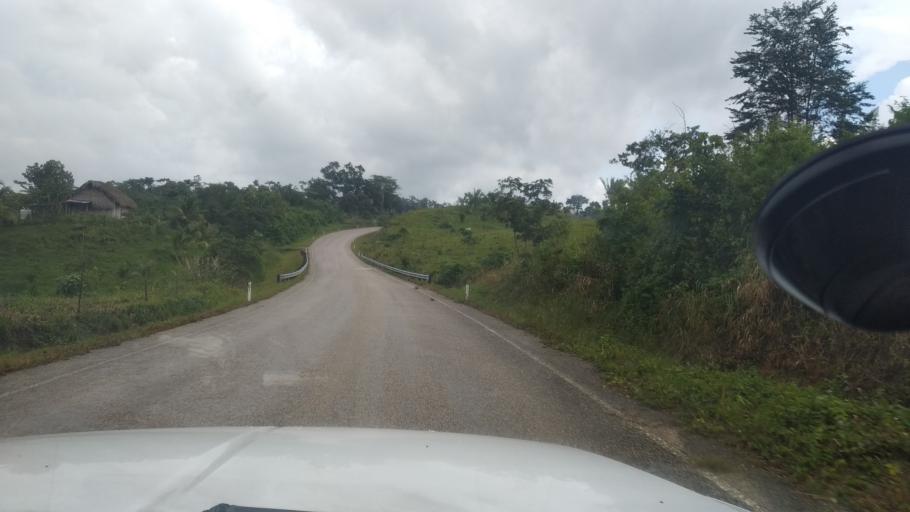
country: GT
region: Peten
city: San Luis
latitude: 16.1988
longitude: -89.1545
